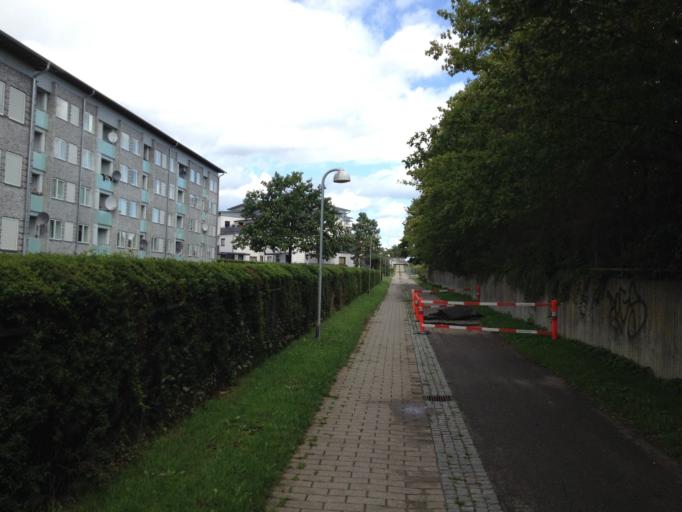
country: DK
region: Capital Region
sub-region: Fredensborg Kommune
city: Niva
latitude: 55.9389
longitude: 12.5026
